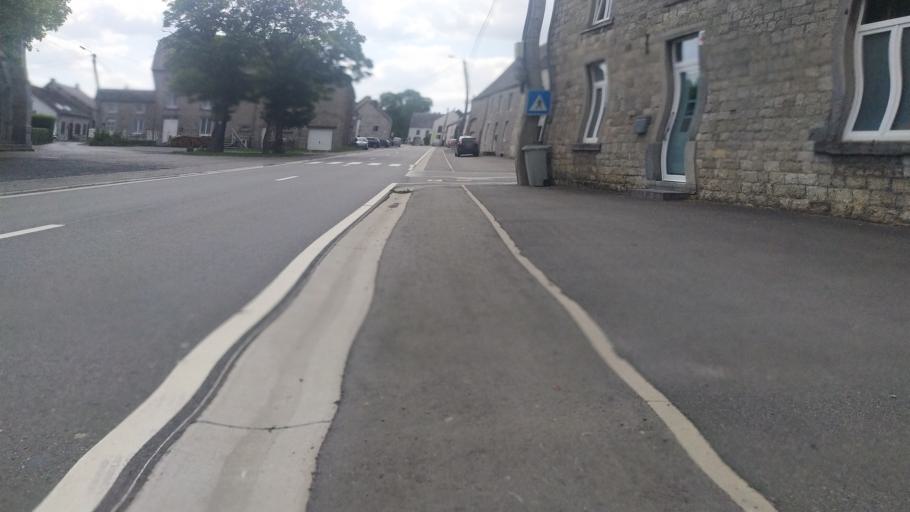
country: BE
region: Wallonia
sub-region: Province du Luxembourg
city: Wellin
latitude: 50.0764
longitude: 5.0926
